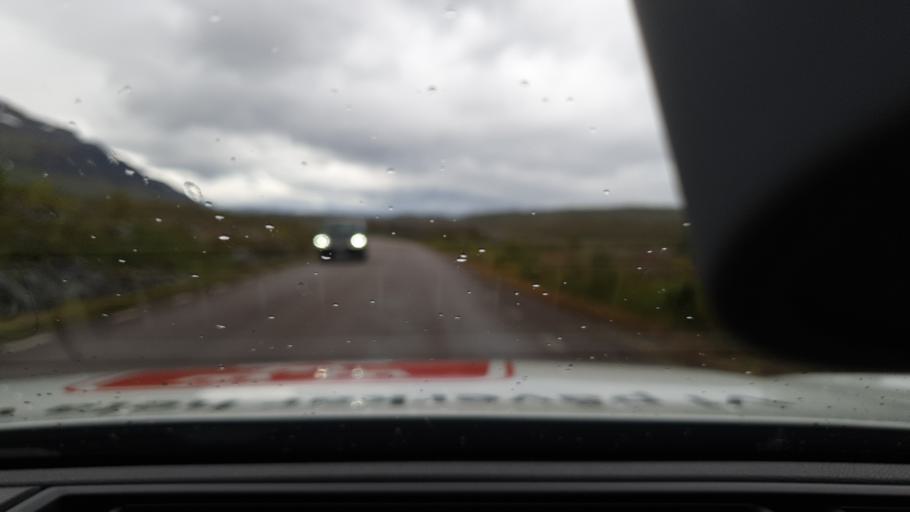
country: NO
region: Troms
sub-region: Bardu
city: Setermoen
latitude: 68.4320
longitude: 18.5370
